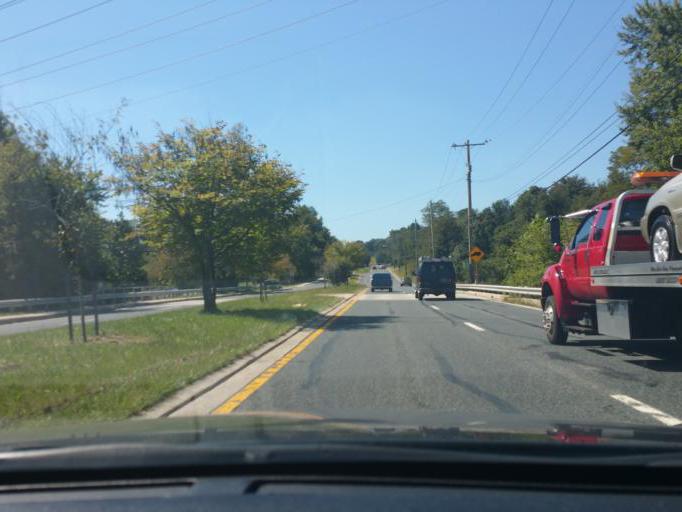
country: US
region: Maryland
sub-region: Harford County
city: South Bel Air
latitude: 39.5421
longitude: -76.3296
